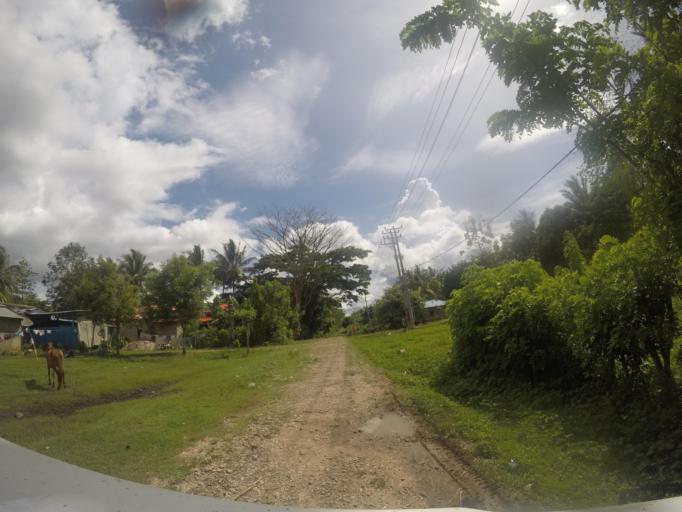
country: TL
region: Lautem
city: Lospalos
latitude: -8.4959
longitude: 127.0096
